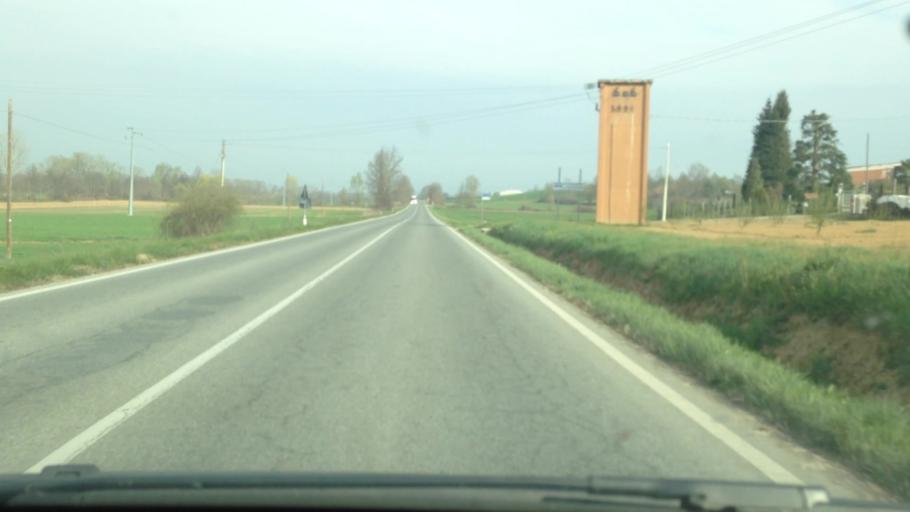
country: IT
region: Piedmont
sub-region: Provincia di Torino
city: Pralormo
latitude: 44.8377
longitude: 7.9154
